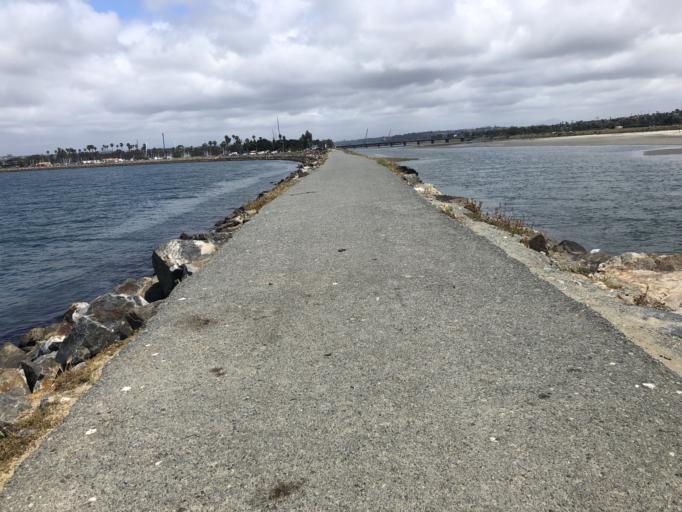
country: US
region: California
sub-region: San Diego County
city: La Jolla
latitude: 32.7574
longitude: -117.2474
